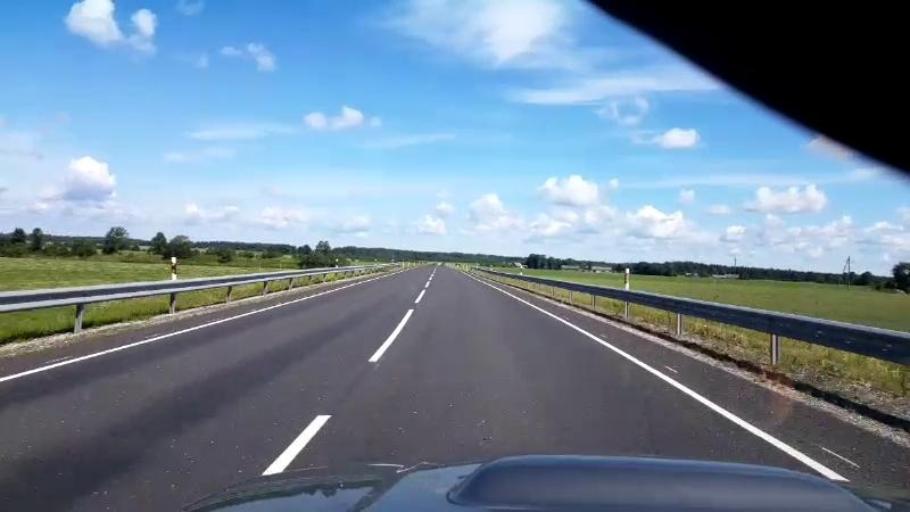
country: EE
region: Jaervamaa
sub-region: Jaerva-Jaani vald
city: Jarva-Jaani
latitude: 59.1426
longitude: 25.7712
